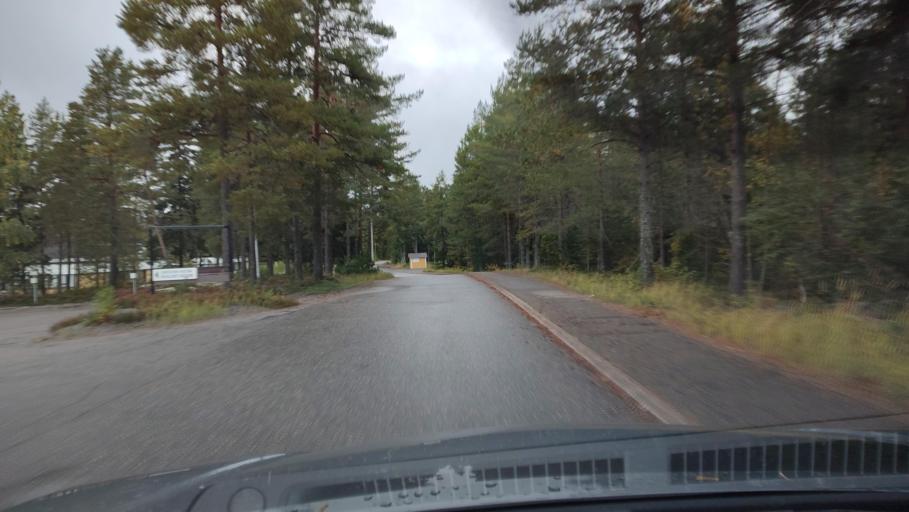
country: FI
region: Ostrobothnia
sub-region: Sydosterbotten
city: Kristinestad
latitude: 62.2721
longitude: 21.4056
